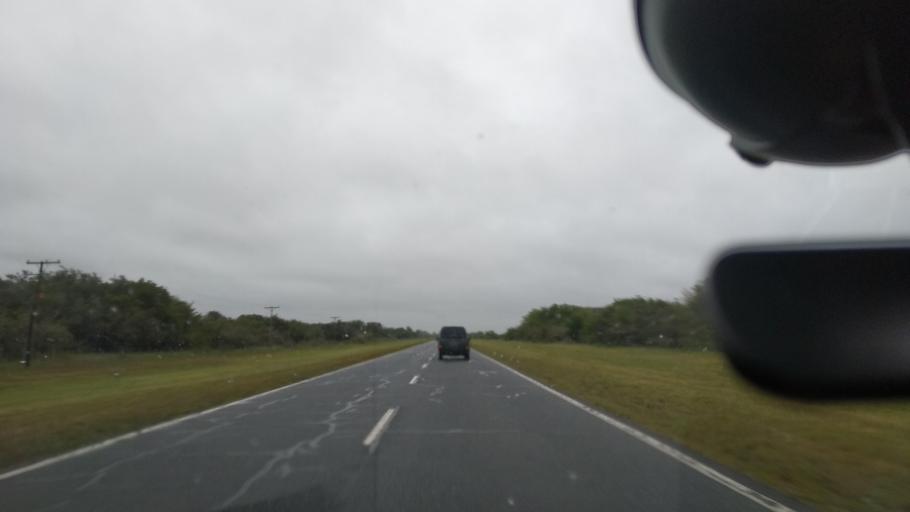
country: AR
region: Buenos Aires
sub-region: Partido de Castelli
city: Castelli
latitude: -35.9231
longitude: -57.4430
